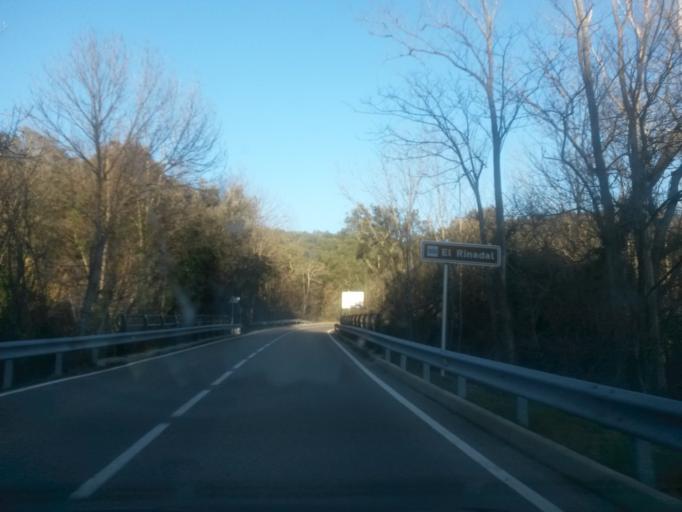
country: ES
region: Catalonia
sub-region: Provincia de Girona
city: Macanet de Cabrenys
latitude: 42.3906
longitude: 2.7643
